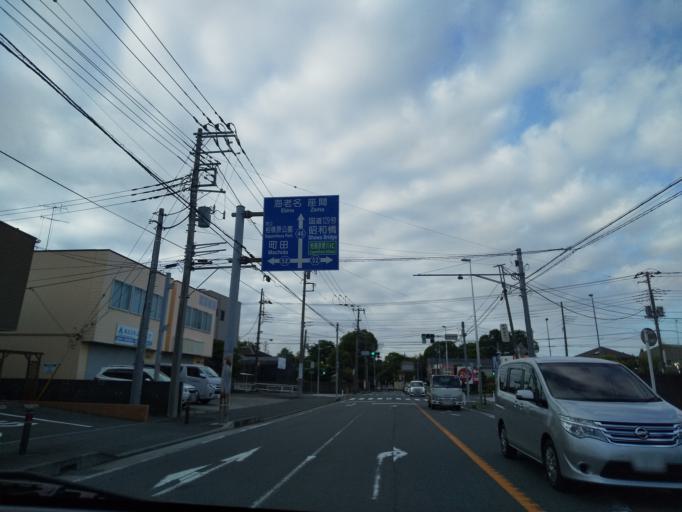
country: JP
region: Kanagawa
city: Zama
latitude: 35.5278
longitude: 139.3743
